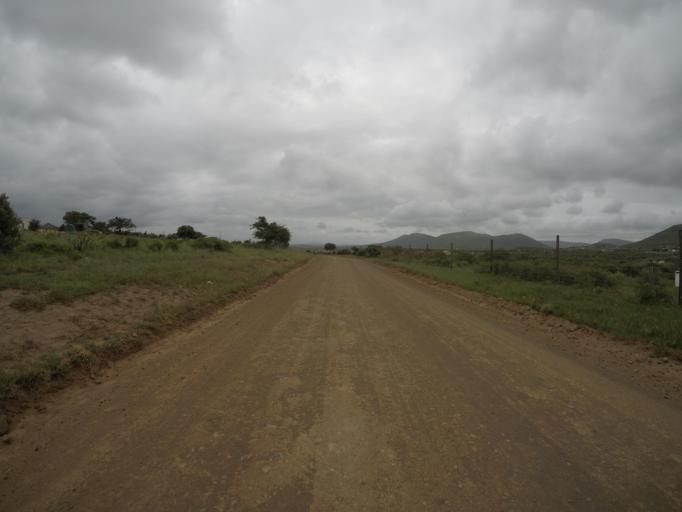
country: ZA
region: KwaZulu-Natal
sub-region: uThungulu District Municipality
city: Empangeni
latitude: -28.5959
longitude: 31.8390
